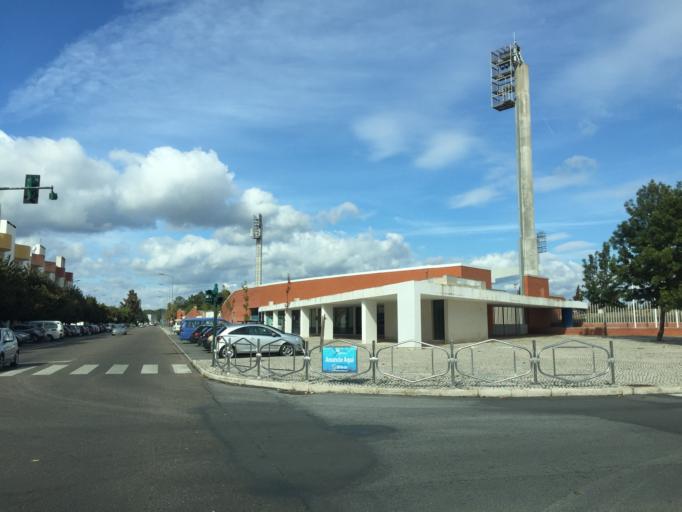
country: PT
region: Portalegre
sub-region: Ponte de Sor
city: Ponte de Sor
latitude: 39.2525
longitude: -8.0138
